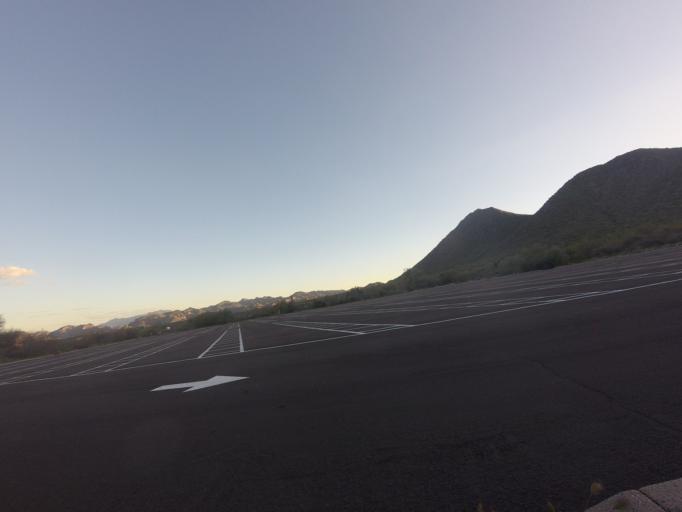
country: US
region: Arizona
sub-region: Maricopa County
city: Fountain Hills
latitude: 33.5948
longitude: -111.5432
